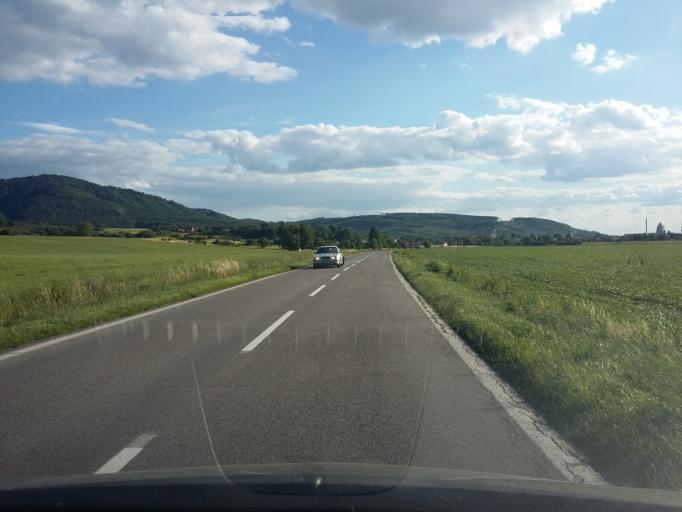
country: SK
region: Bratislavsky
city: Modra
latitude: 48.4730
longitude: 17.2432
